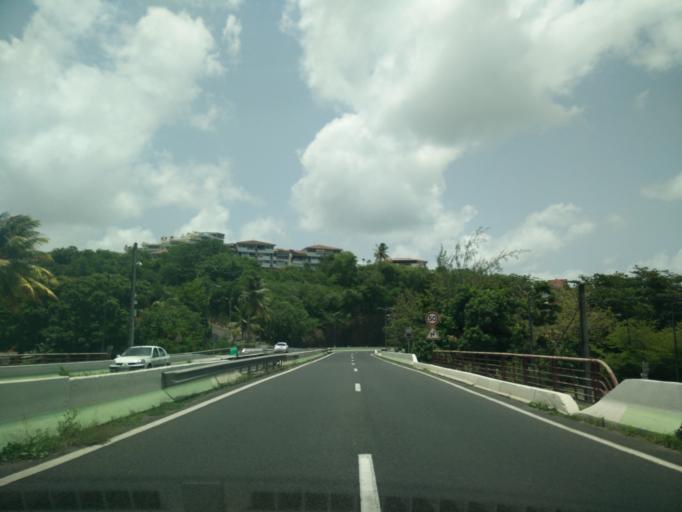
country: MQ
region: Martinique
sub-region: Martinique
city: Fort-de-France
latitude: 14.6143
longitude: -61.0974
